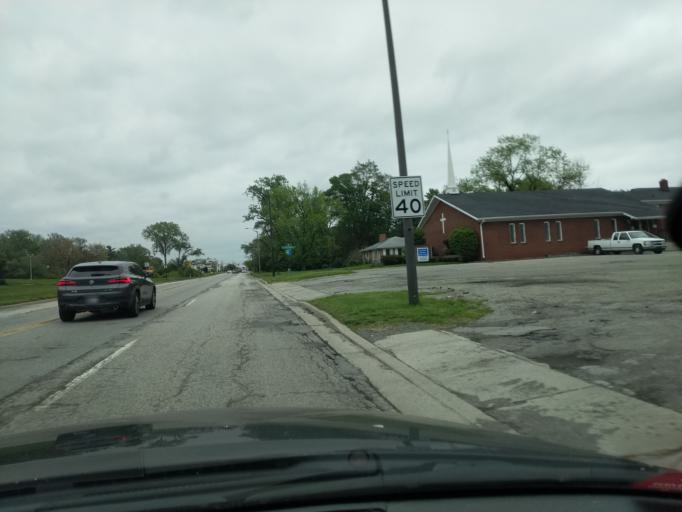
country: US
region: Indiana
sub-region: Marion County
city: Warren Park
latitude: 39.8254
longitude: -86.0887
